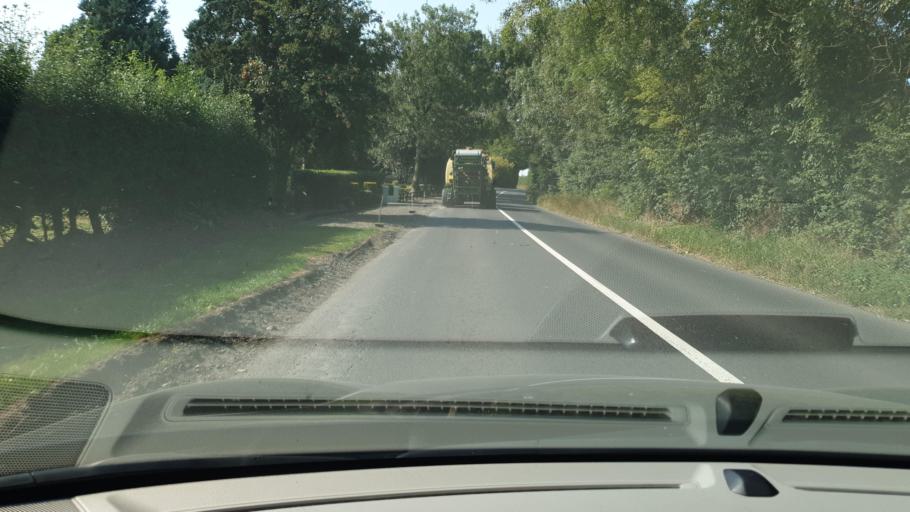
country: IE
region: Leinster
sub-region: An Mhi
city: Athboy
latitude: 53.6177
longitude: -6.9076
